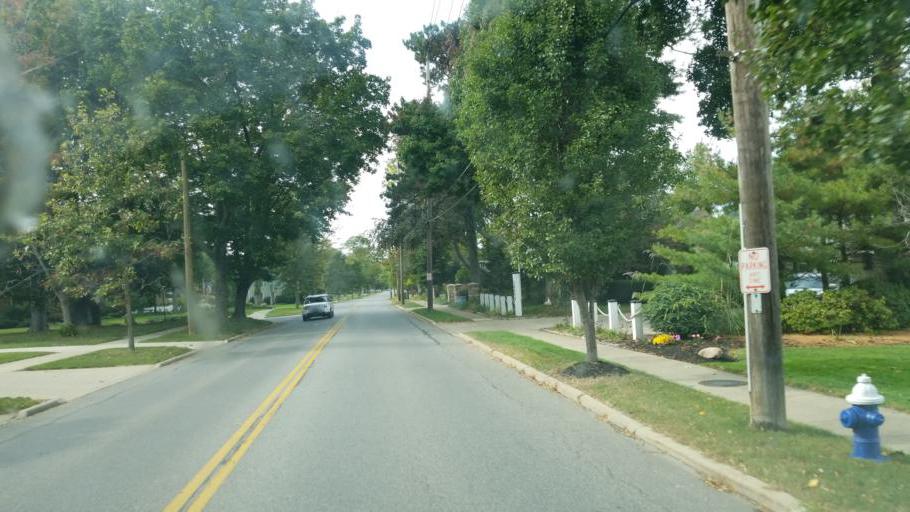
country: US
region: Ohio
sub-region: Cuyahoga County
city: Bay Village
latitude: 41.4907
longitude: -81.9389
